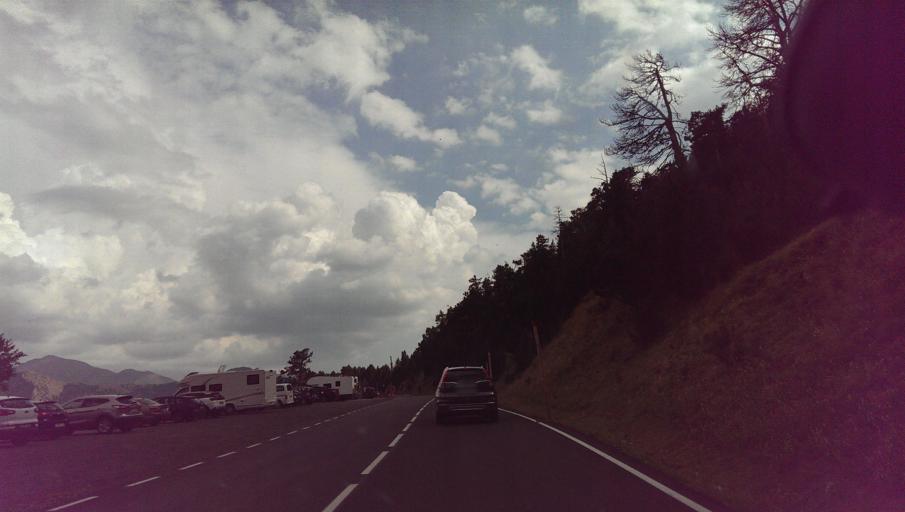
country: AD
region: Canillo
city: Canillo
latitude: 42.5715
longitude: 1.5866
